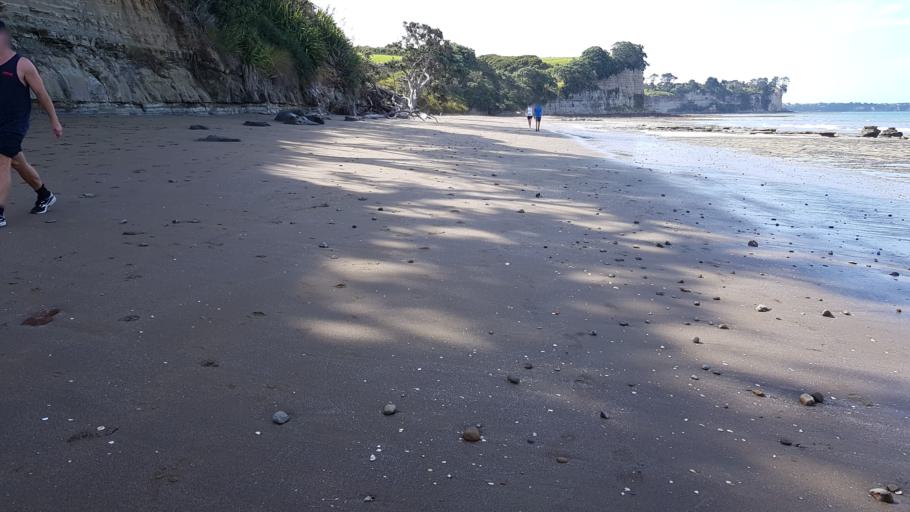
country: NZ
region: Auckland
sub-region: Auckland
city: Rothesay Bay
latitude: -36.6758
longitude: 174.7480
